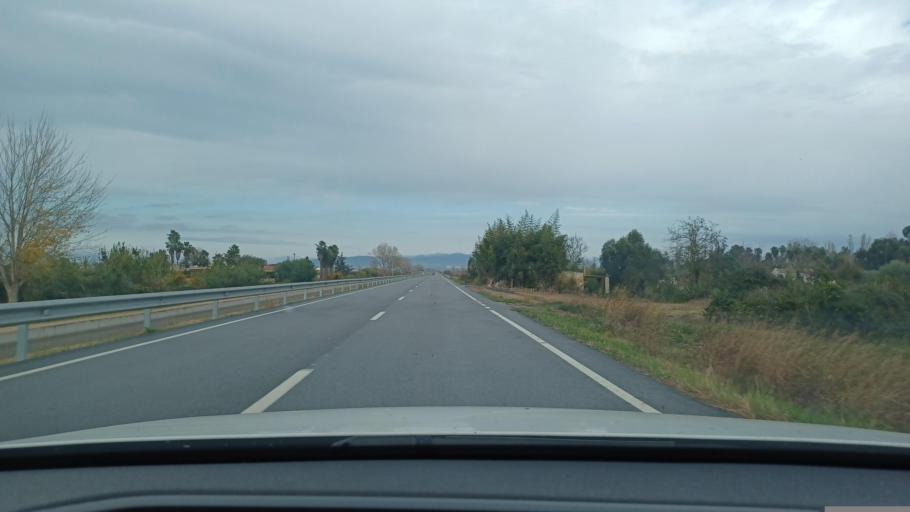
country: ES
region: Catalonia
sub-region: Provincia de Tarragona
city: Amposta
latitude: 40.6749
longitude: 0.5906
